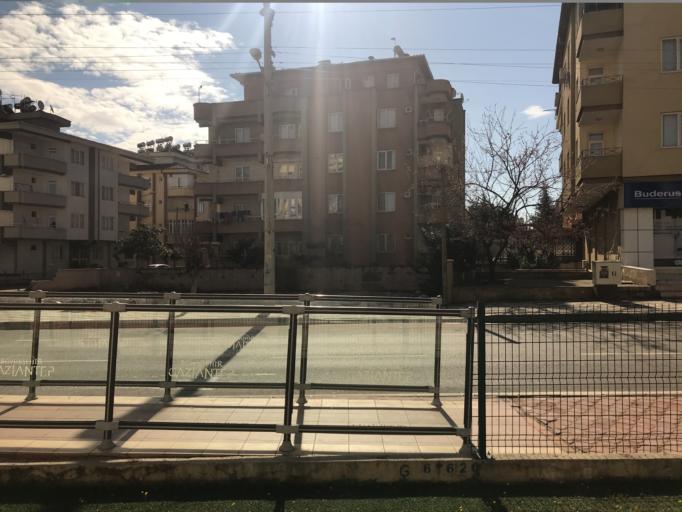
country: TR
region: Gaziantep
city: Sahinbey
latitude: 37.0478
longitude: 37.3258
